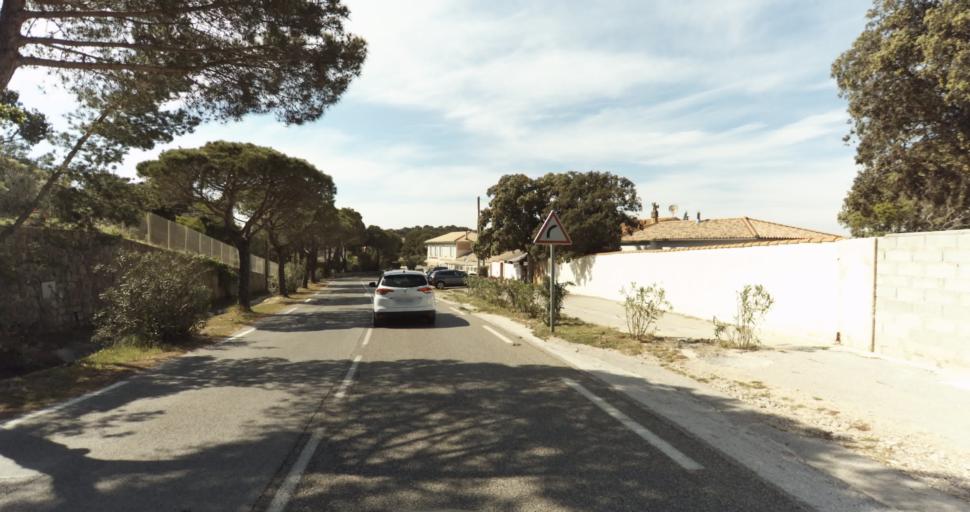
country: FR
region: Provence-Alpes-Cote d'Azur
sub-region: Departement du Var
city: Hyeres
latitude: 43.0345
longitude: 6.1450
